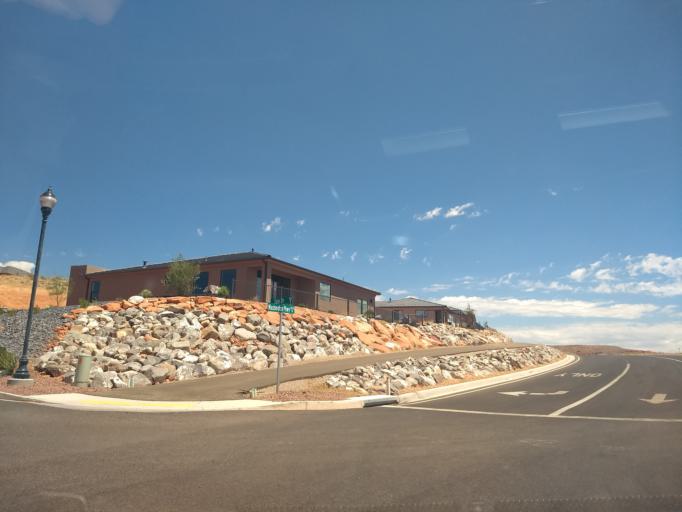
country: US
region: Utah
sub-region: Washington County
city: Washington
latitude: 37.1591
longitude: -113.5263
